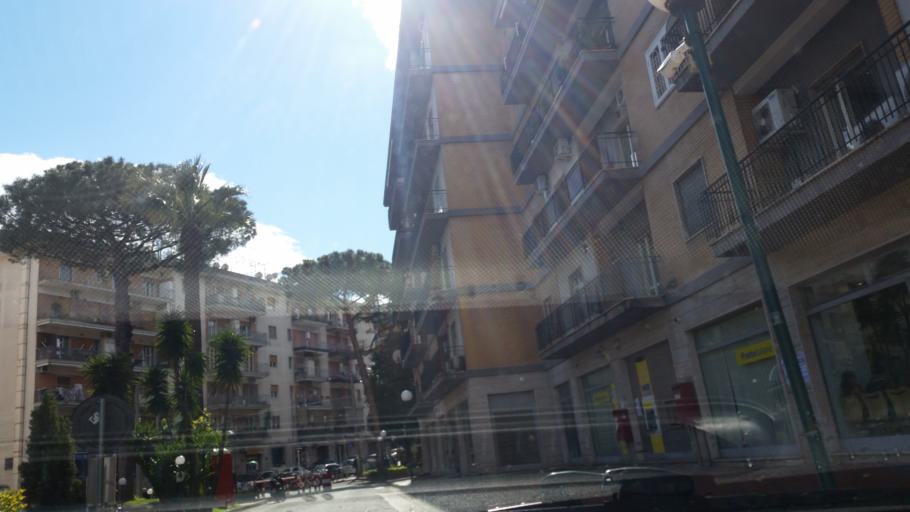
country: IT
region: Campania
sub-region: Provincia di Napoli
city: Napoli
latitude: 40.8717
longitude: 14.2397
